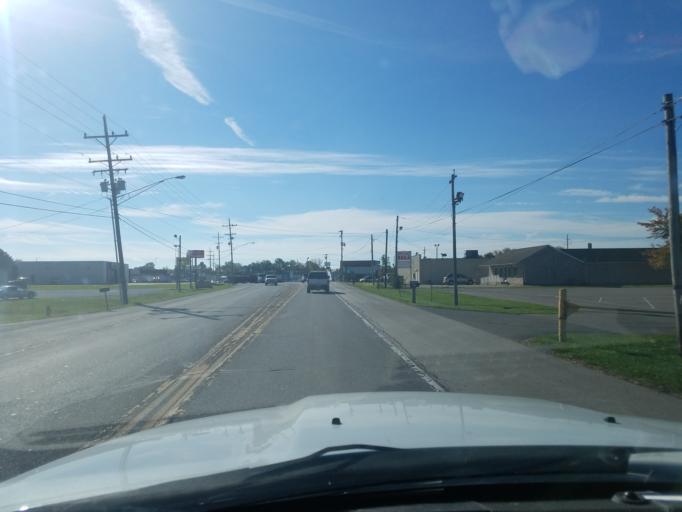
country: US
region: Indiana
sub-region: Jennings County
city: North Vernon
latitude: 39.0174
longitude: -85.6400
